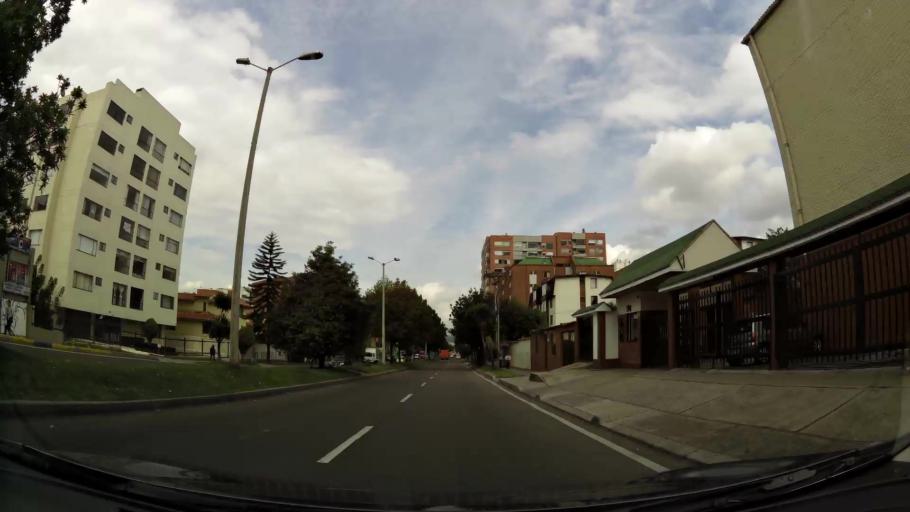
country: CO
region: Bogota D.C.
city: Barrio San Luis
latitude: 4.7240
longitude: -74.0289
